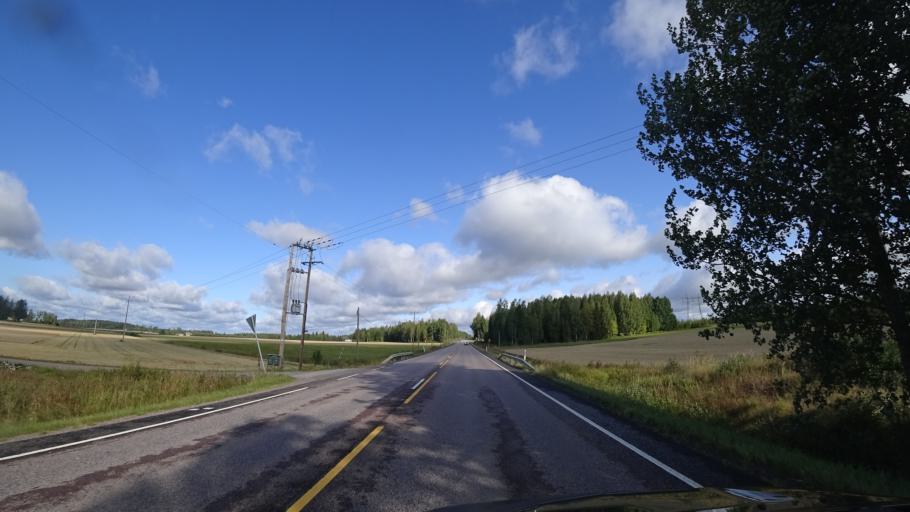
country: FI
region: Uusimaa
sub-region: Helsinki
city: Nurmijaervi
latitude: 60.5015
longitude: 24.9336
